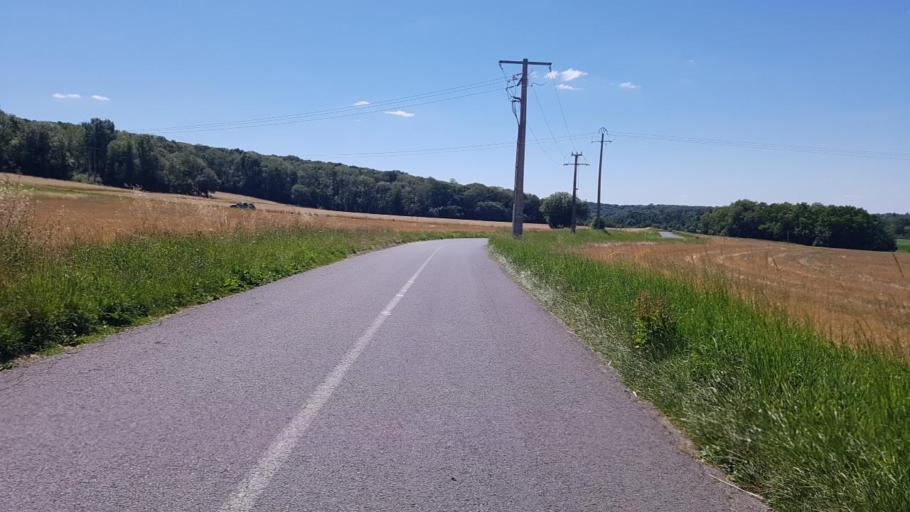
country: FR
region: Ile-de-France
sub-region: Departement de Seine-et-Marne
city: Fublaines
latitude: 48.9395
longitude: 2.9291
